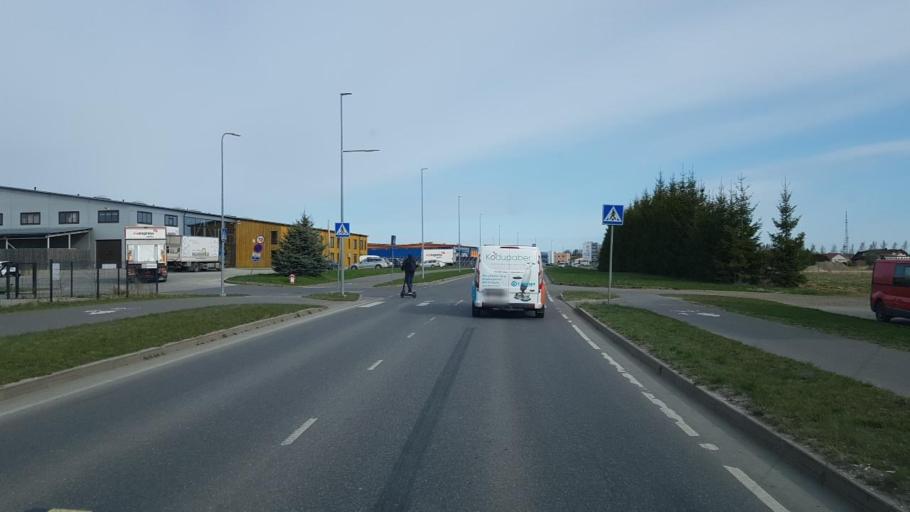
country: EE
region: Tartu
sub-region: UElenurme vald
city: Ulenurme
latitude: 58.3345
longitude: 26.7046
